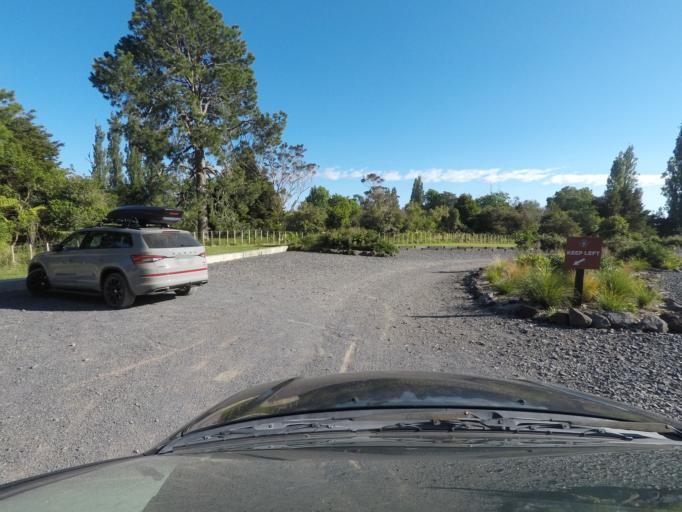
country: NZ
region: Northland
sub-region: Far North District
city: Paihia
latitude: -35.2529
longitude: 174.0700
